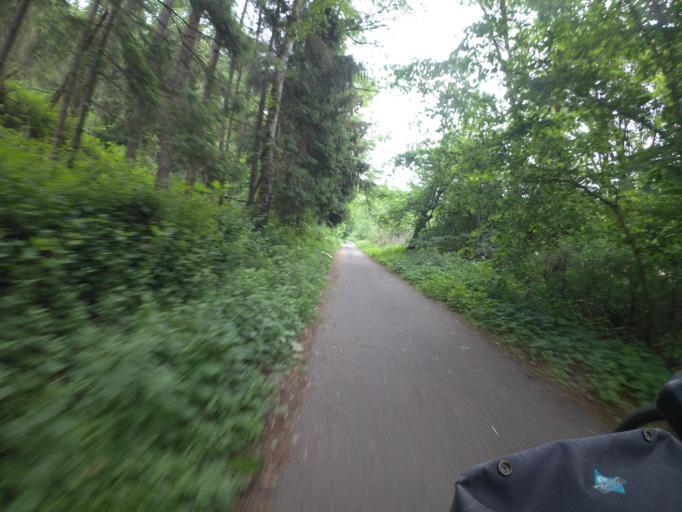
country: DE
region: Rheinland-Pfalz
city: Donsieders
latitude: 49.2738
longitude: 7.6201
